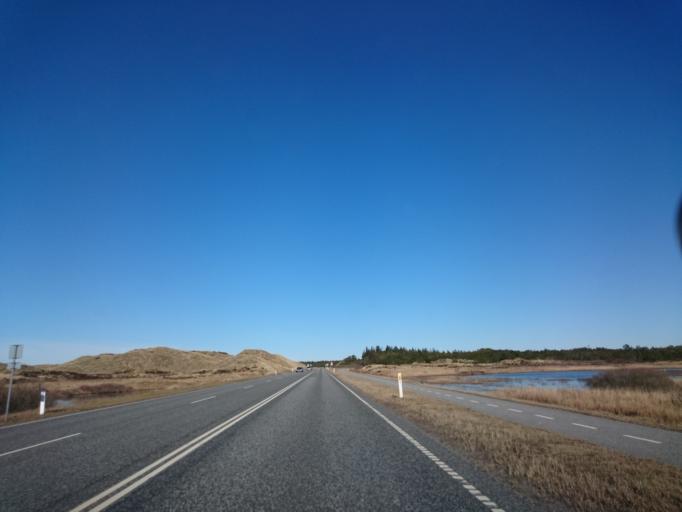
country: DK
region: North Denmark
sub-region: Frederikshavn Kommune
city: Skagen
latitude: 57.6930
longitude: 10.4740
